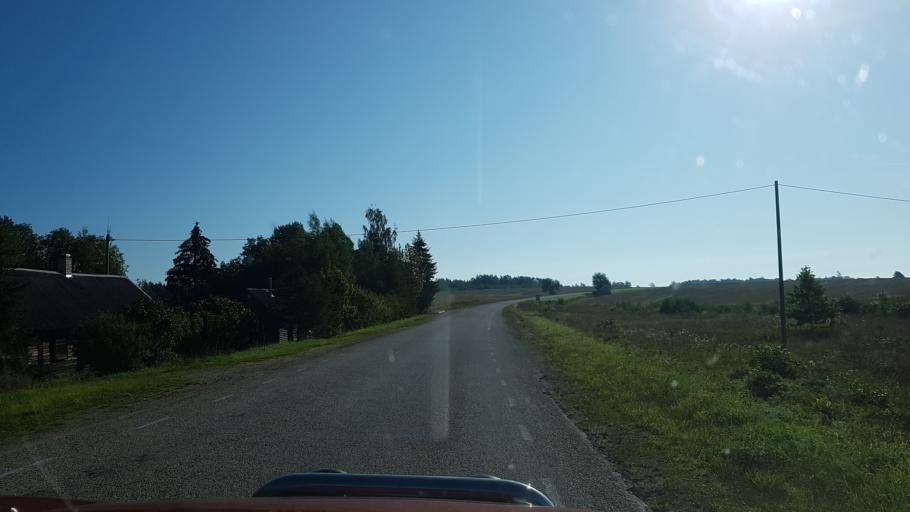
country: EE
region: Jogevamaa
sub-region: Tabivere vald
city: Tabivere
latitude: 58.6775
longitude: 26.7327
